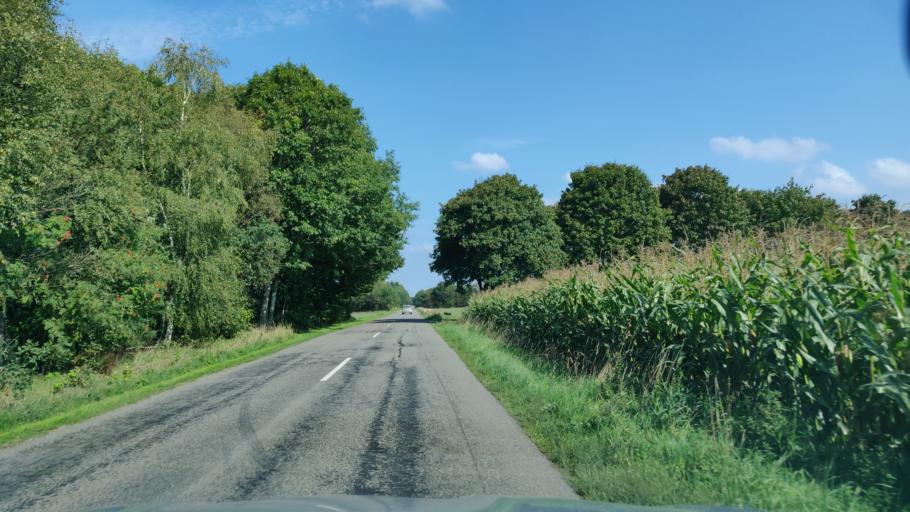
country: DK
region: Central Jutland
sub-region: Herning Kommune
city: Avlum
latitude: 56.2262
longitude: 8.8625
